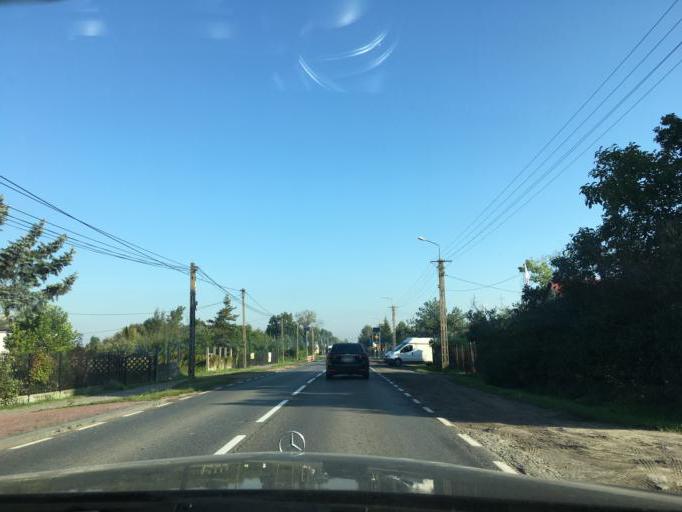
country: PL
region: Masovian Voivodeship
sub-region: Powiat grodziski
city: Grodzisk Mazowiecki
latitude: 52.1327
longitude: 20.6178
